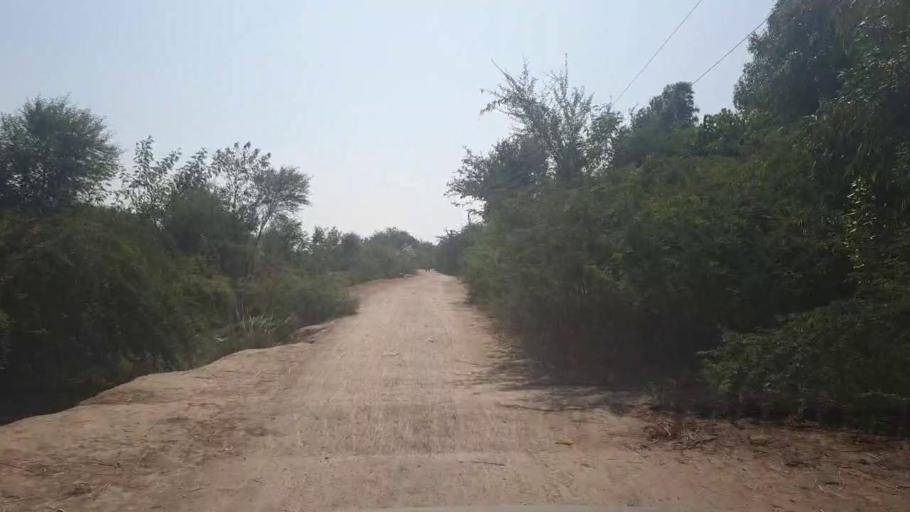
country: PK
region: Sindh
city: Badin
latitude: 24.6823
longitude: 68.8787
